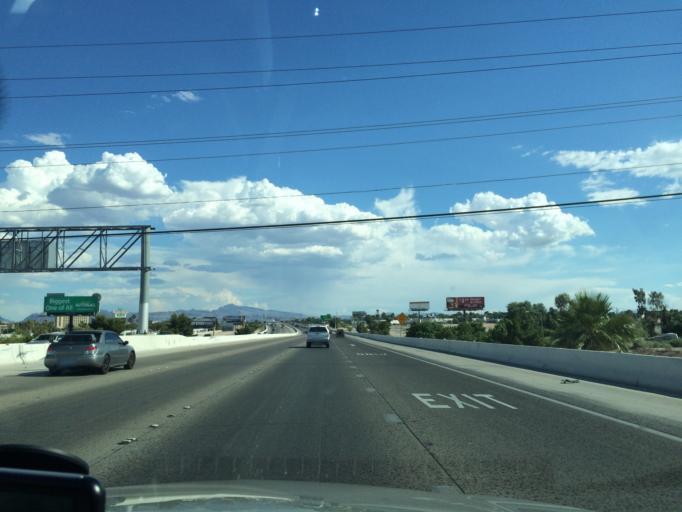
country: US
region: Nevada
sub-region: Clark County
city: Winchester
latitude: 36.1451
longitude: -115.0915
